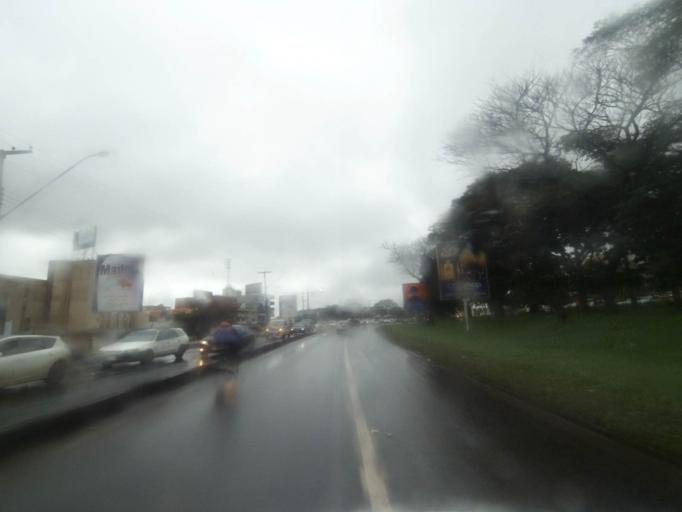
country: PY
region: Alto Parana
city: Ciudad del Este
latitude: -25.5089
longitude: -54.5930
